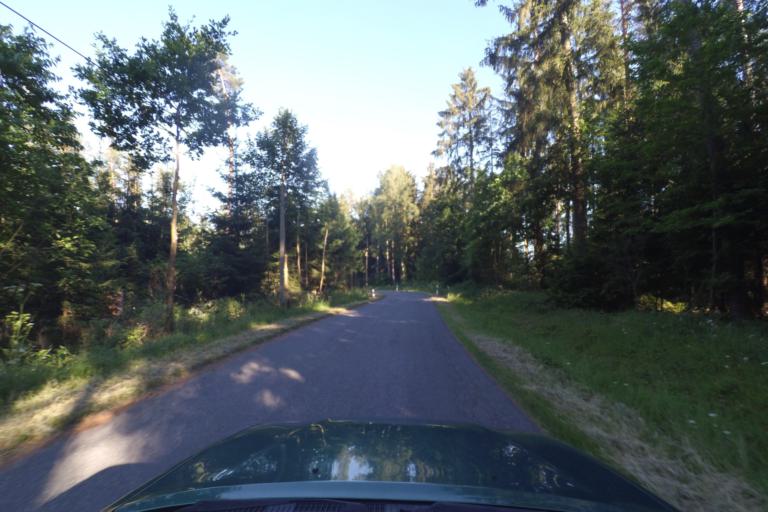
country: DE
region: Bavaria
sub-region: Upper Palatinate
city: Speinshart
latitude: 49.7937
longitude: 11.8237
